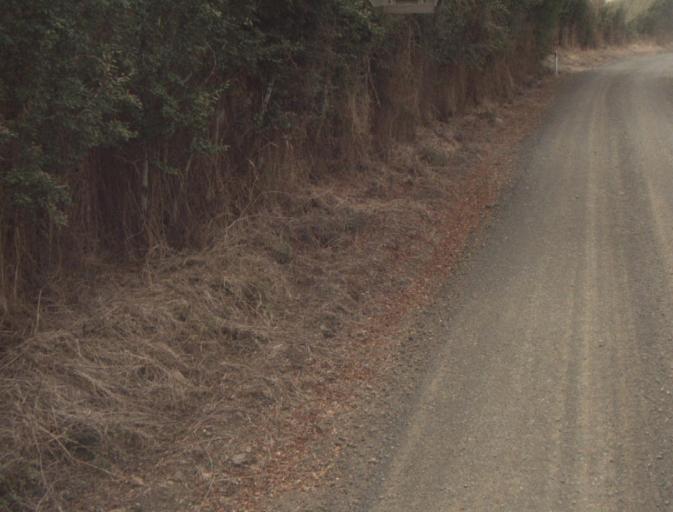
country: AU
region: Tasmania
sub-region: Northern Midlands
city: Evandale
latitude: -41.5245
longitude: 147.2802
